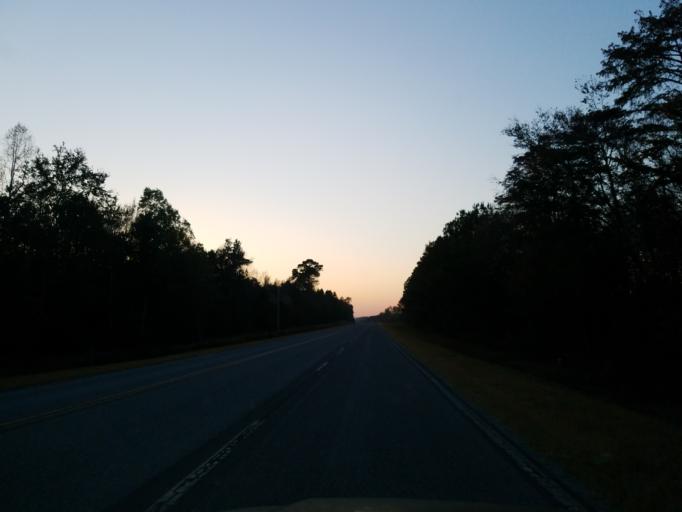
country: US
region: Georgia
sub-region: Ben Hill County
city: Fitzgerald
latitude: 31.7206
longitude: -83.4243
